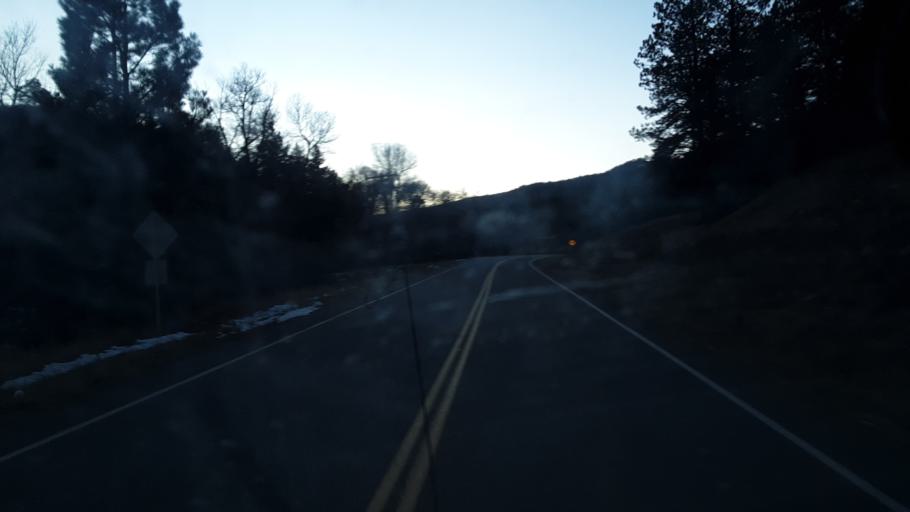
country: US
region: Colorado
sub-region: La Plata County
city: Bayfield
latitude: 37.3462
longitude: -107.7009
